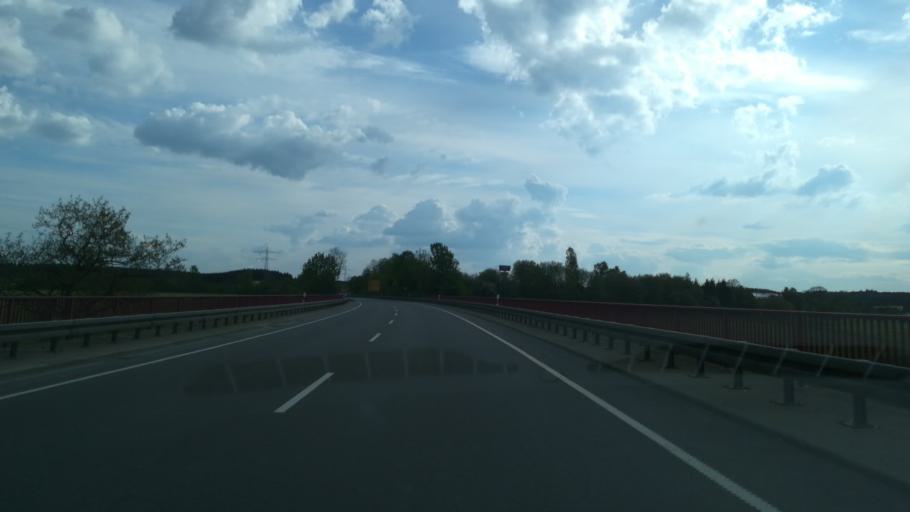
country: DE
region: Baden-Wuerttemberg
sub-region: Tuebingen Region
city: Messkirch
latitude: 47.9953
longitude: 9.0846
